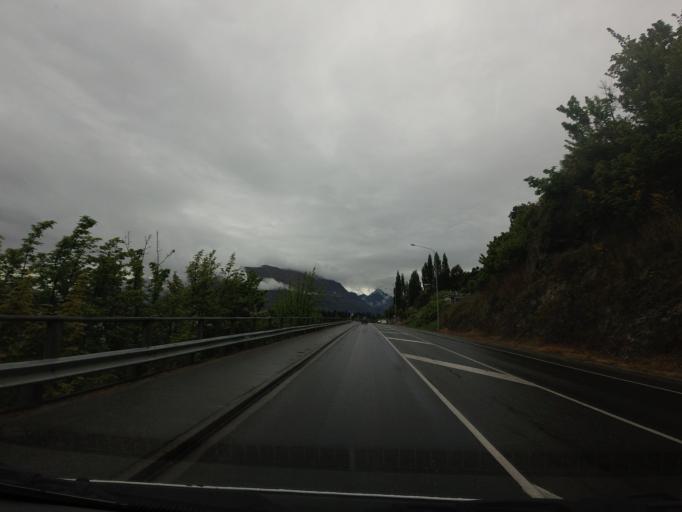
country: NZ
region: Otago
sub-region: Queenstown-Lakes District
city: Queenstown
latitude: -45.0323
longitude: 168.6830
